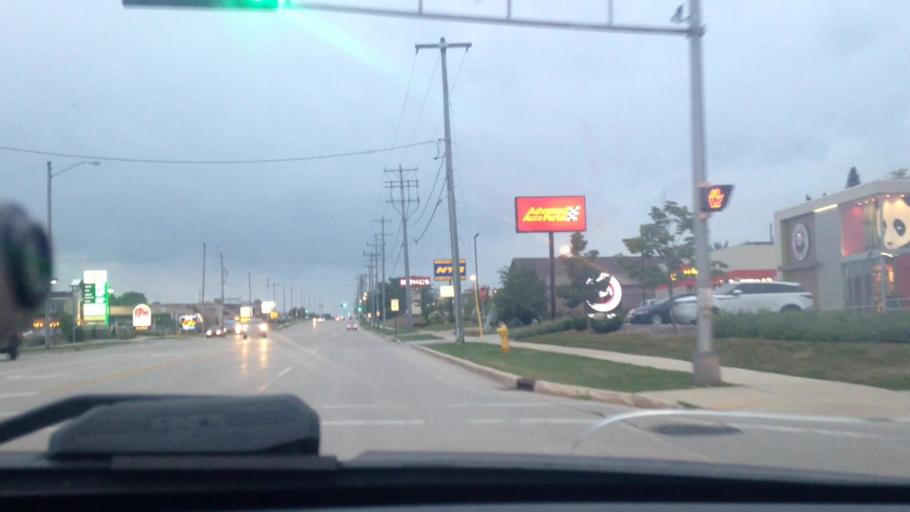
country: US
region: Wisconsin
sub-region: Washington County
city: West Bend
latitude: 43.4050
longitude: -88.1813
